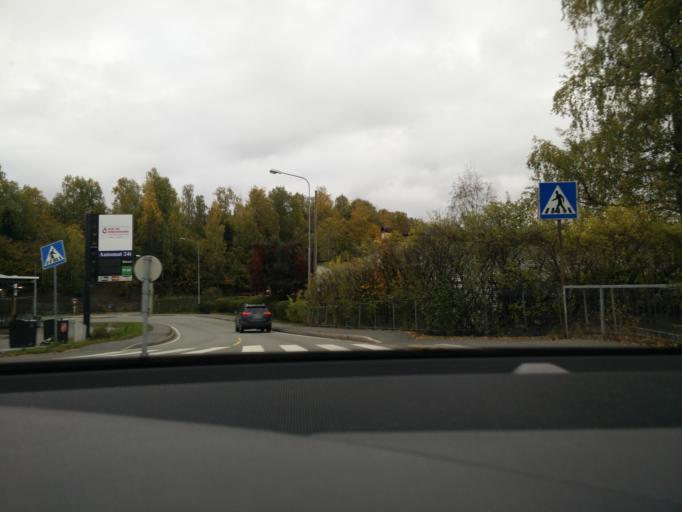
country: NO
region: Akershus
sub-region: Baerum
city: Lysaker
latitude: 59.9368
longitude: 10.6078
